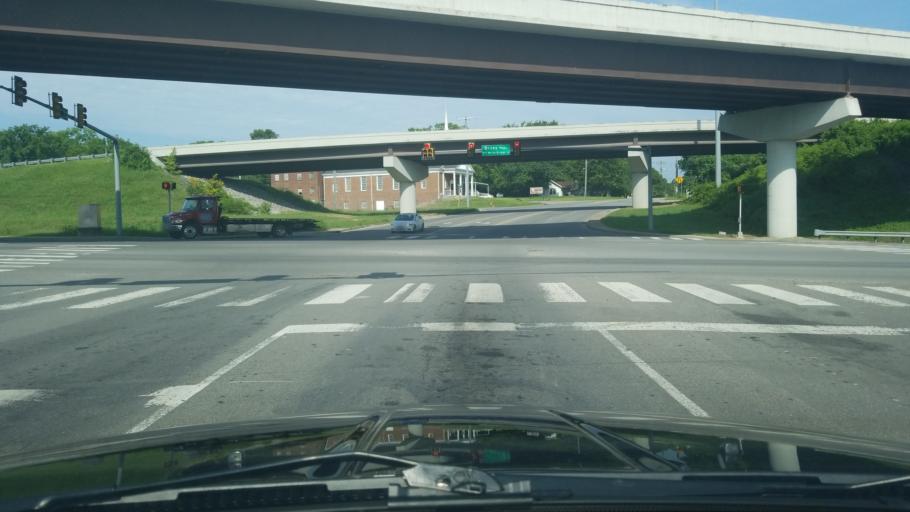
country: US
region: Tennessee
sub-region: Davidson County
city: Belle Meade
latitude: 36.1539
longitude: -86.8572
